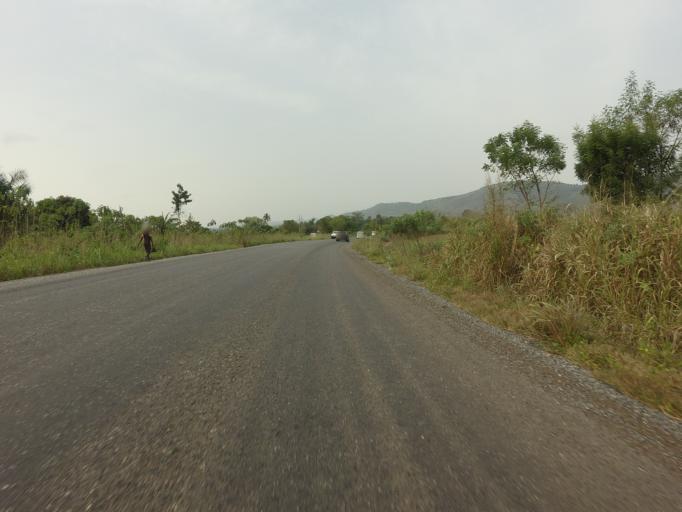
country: GH
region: Volta
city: Ho
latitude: 6.4412
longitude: 0.2057
